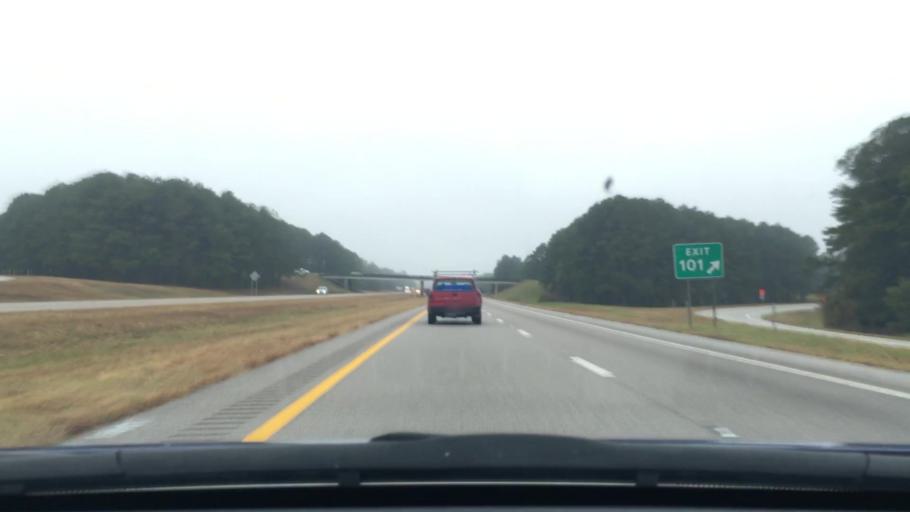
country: US
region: South Carolina
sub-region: Kershaw County
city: Camden
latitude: 34.2161
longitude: -80.5266
